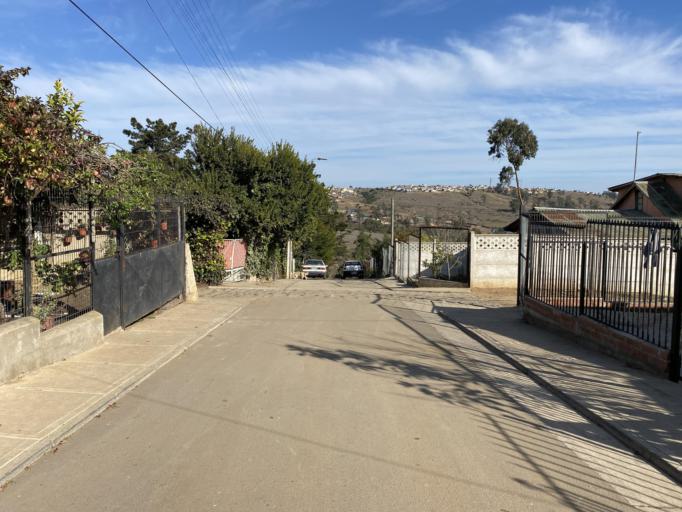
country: CL
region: Valparaiso
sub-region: San Antonio Province
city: Cartagena
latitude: -33.5522
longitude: -71.5890
